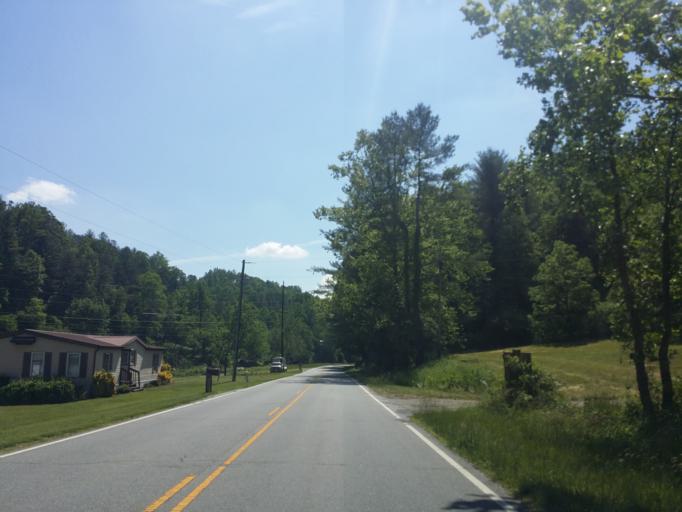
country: US
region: North Carolina
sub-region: Madison County
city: Marshall
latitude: 35.7074
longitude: -82.7742
